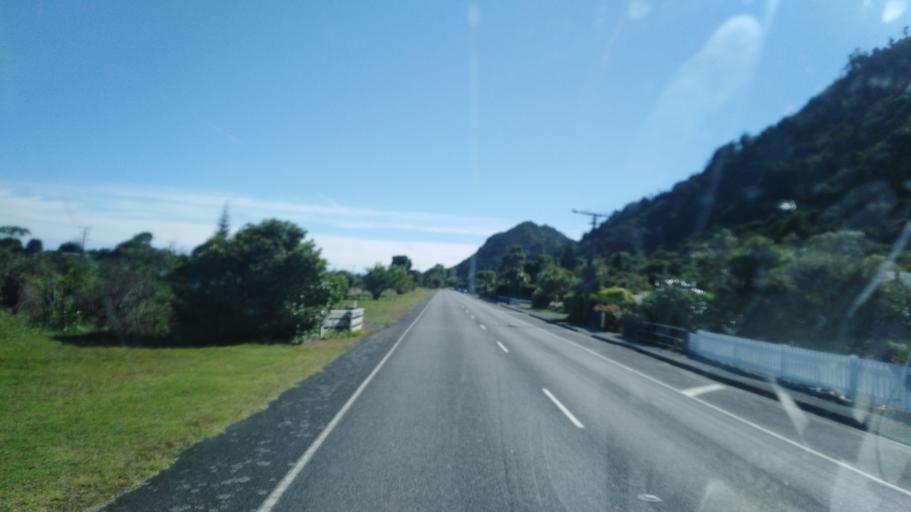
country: NZ
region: West Coast
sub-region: Buller District
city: Westport
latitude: -41.6352
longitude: 171.8495
